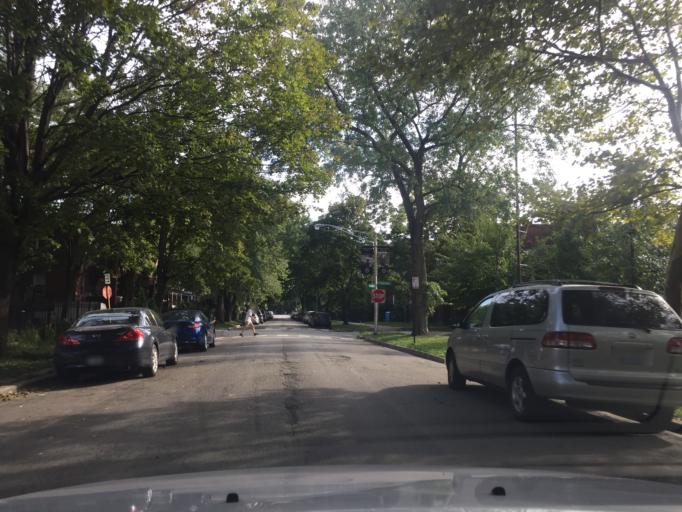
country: US
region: Illinois
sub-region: Cook County
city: Lincolnwood
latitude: 41.9635
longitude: -87.6912
